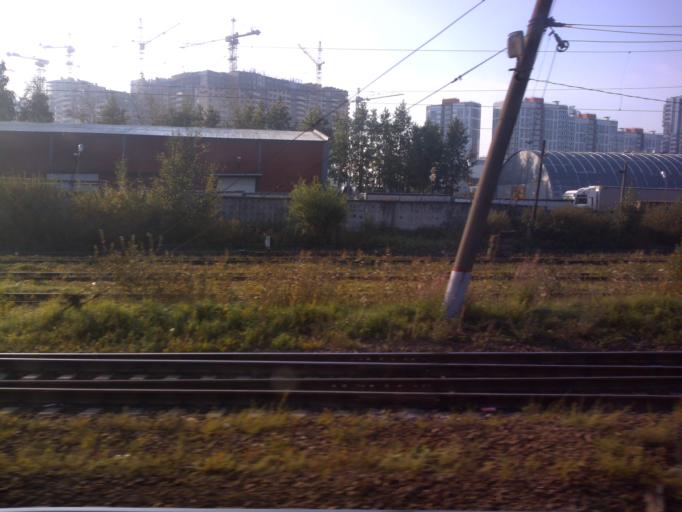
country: RU
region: St.-Petersburg
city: Kushelevka
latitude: 59.9914
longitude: 30.3717
